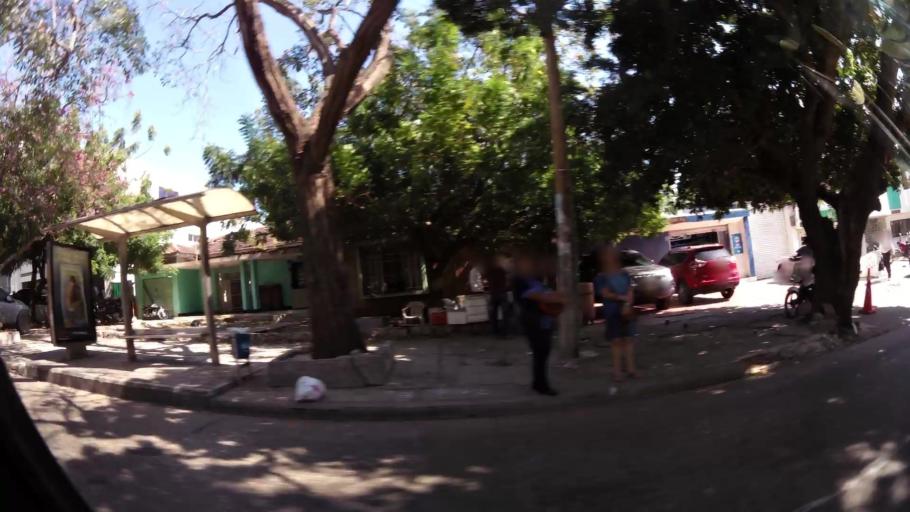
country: CO
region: Atlantico
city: Barranquilla
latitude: 10.9954
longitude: -74.7962
